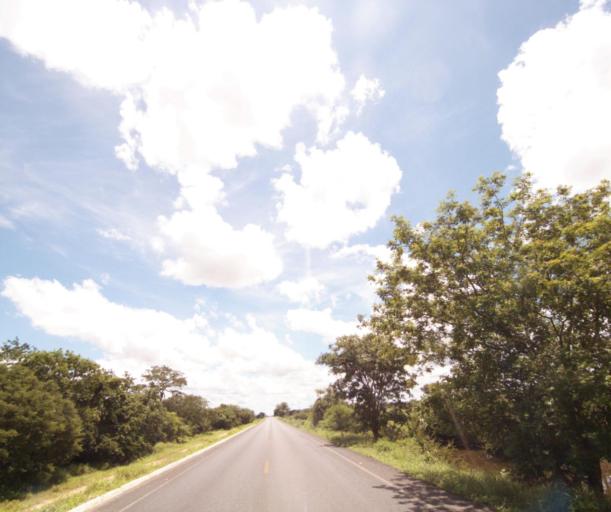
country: BR
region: Bahia
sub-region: Bom Jesus Da Lapa
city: Bom Jesus da Lapa
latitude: -13.2587
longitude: -43.4811
